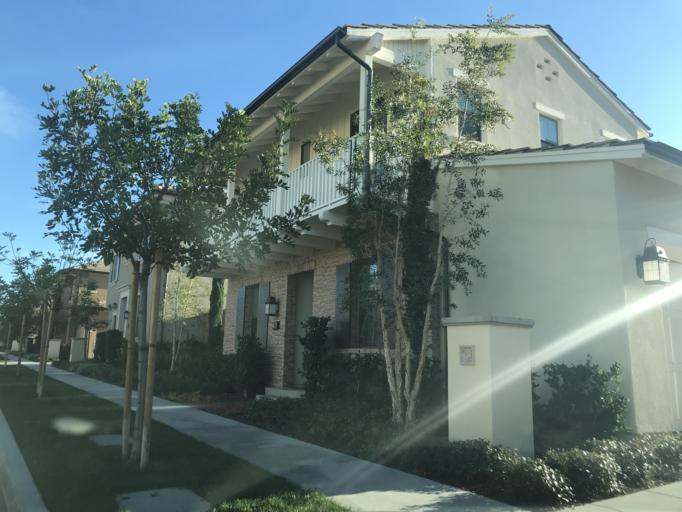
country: US
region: California
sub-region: Orange County
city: North Tustin
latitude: 33.7142
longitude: -117.7551
